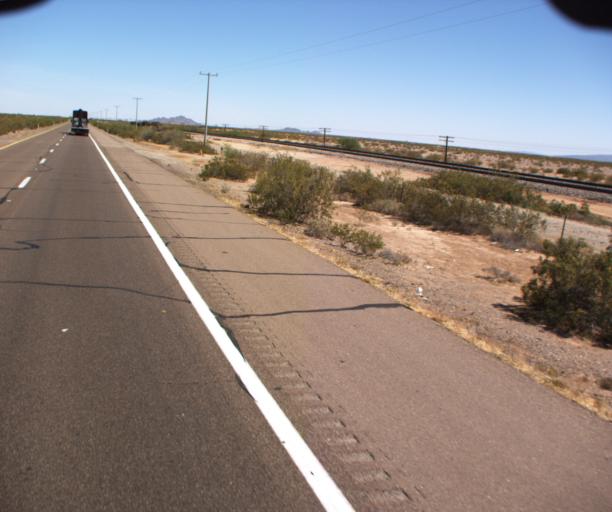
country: US
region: Arizona
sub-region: Yuma County
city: Wellton
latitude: 32.7605
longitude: -113.6351
